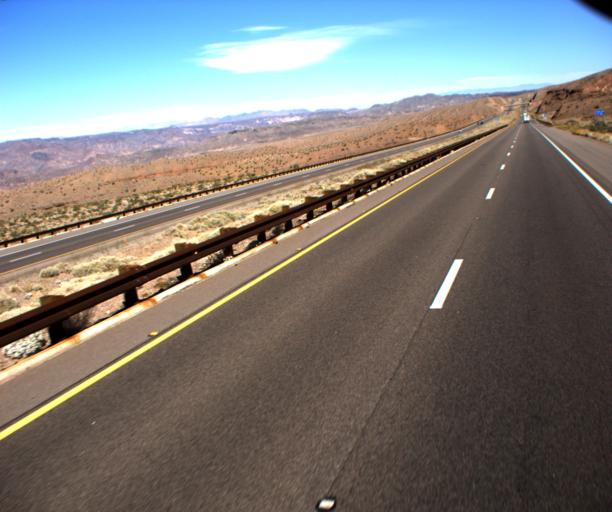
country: US
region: Nevada
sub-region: Clark County
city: Boulder City
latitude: 35.8767
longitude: -114.6122
